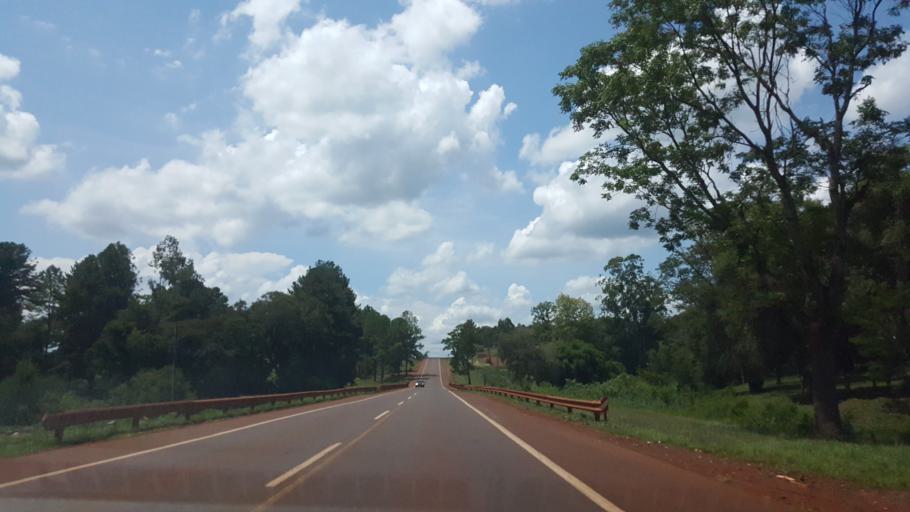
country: AR
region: Misiones
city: Garuhape
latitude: -26.8161
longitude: -54.9473
